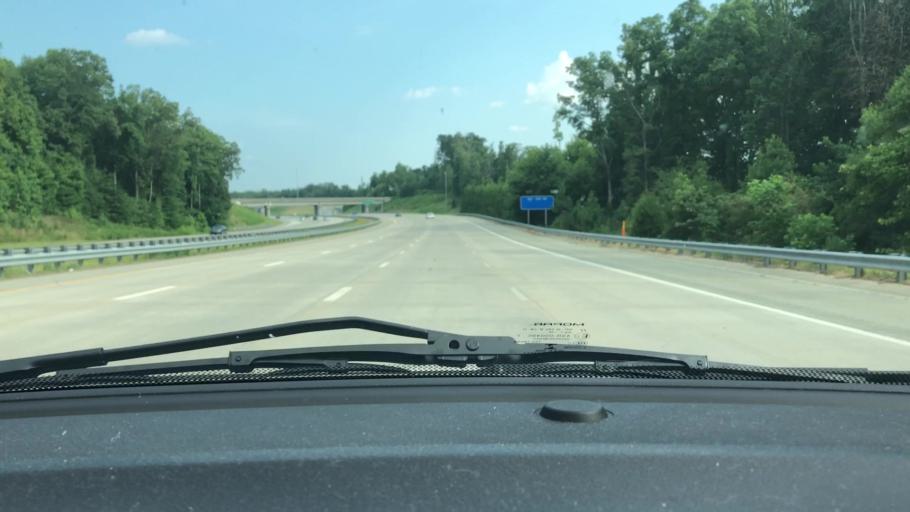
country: US
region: North Carolina
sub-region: Guilford County
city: Jamestown
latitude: 36.0331
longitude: -79.8889
